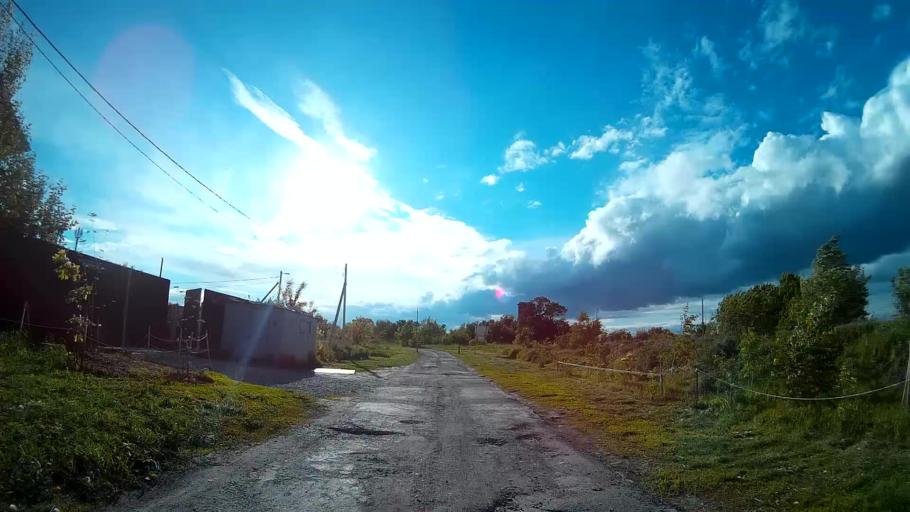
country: RU
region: Ulyanovsk
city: Novoul'yanovsk
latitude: 54.2048
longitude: 48.2718
